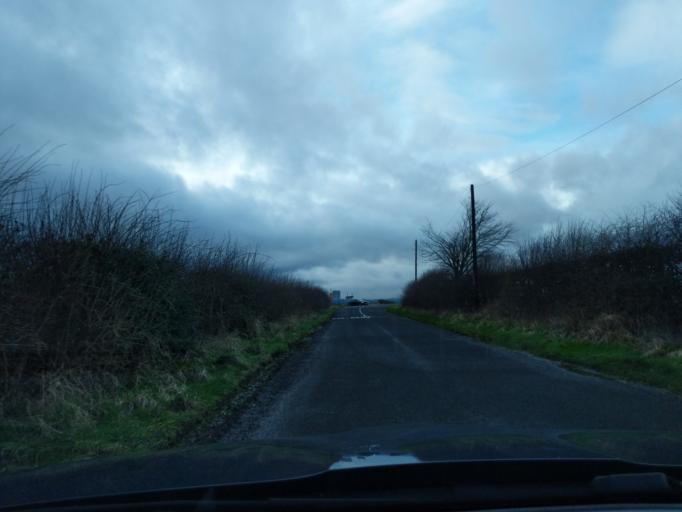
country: GB
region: England
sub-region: Northumberland
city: Ford
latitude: 55.7128
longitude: -2.1206
